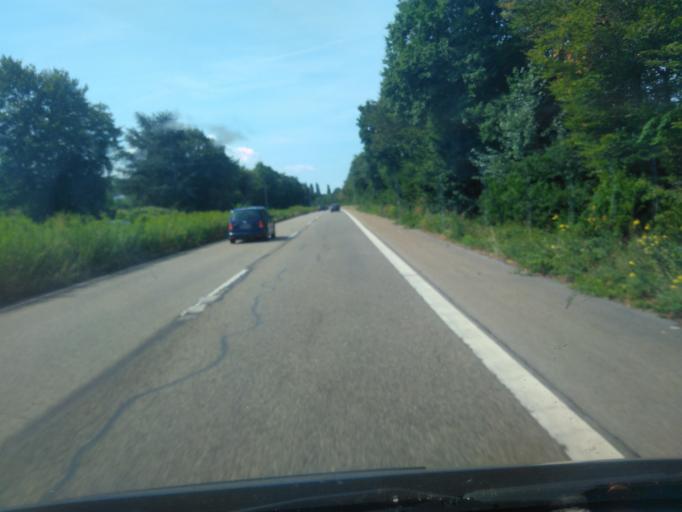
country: DE
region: Baden-Wuerttemberg
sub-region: Freiburg Region
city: Gundelfingen
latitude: 48.0301
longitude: 7.8595
